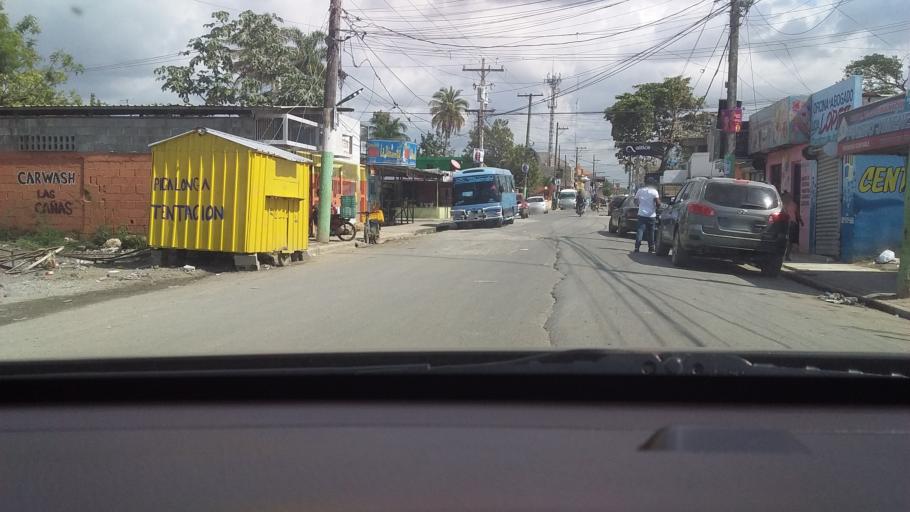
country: DO
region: Santo Domingo
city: Guerra
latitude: 18.5575
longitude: -69.7018
